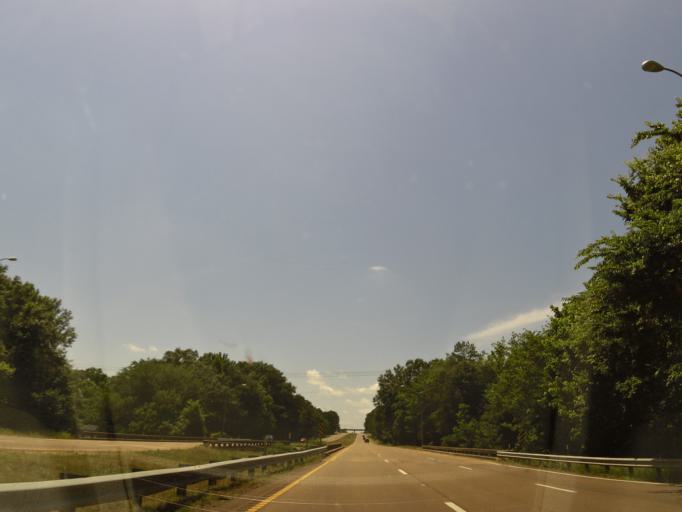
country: US
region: Mississippi
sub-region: Lafayette County
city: Oxford
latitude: 34.3542
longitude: -89.5119
